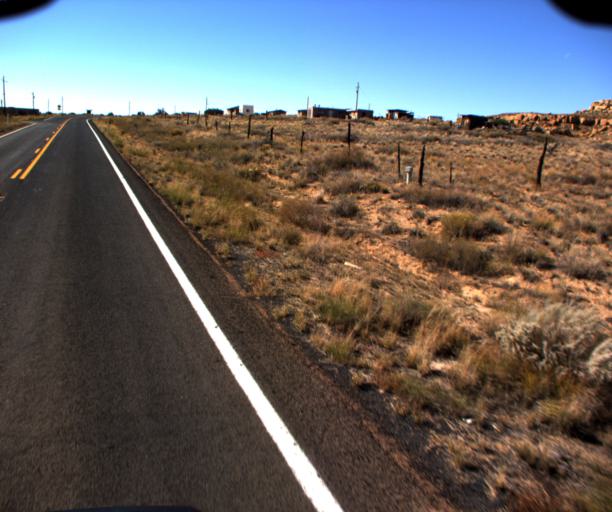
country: US
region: Arizona
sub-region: Navajo County
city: First Mesa
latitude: 35.8820
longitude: -110.6415
